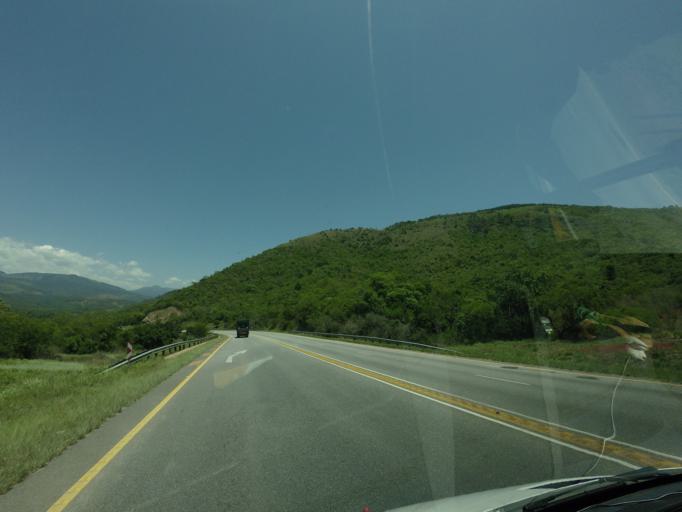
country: ZA
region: Mpumalanga
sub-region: Ehlanzeni District
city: Nelspruit
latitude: -25.4451
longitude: 30.7168
